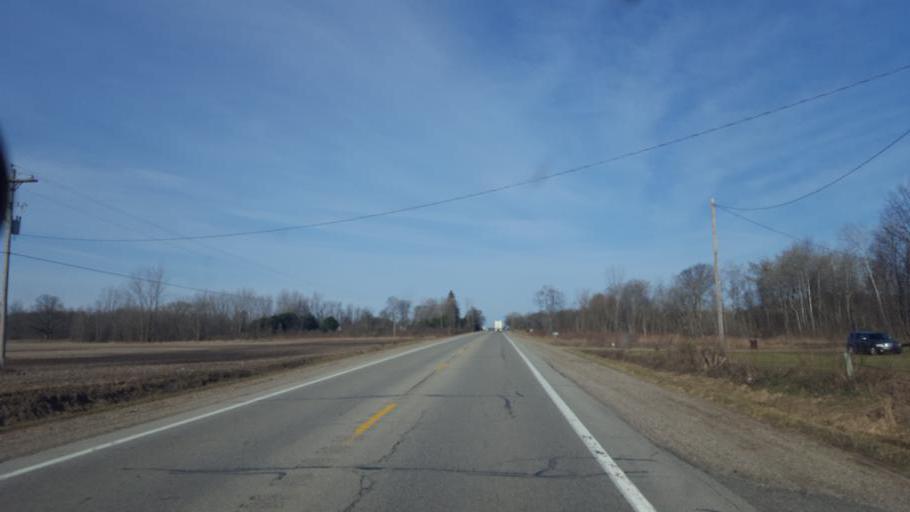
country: US
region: Michigan
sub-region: Montcalm County
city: Lakeview
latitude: 43.4301
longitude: -85.1749
